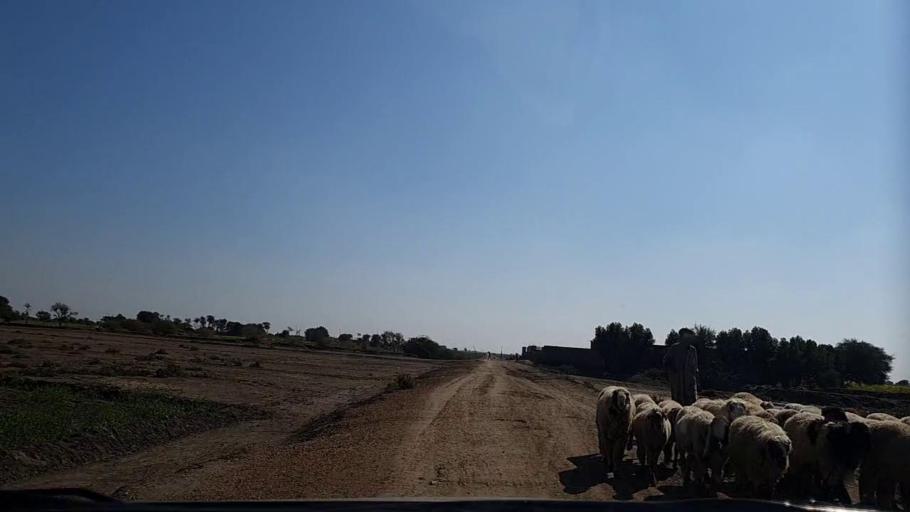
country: PK
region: Sindh
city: Pithoro
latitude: 25.7084
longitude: 69.3351
